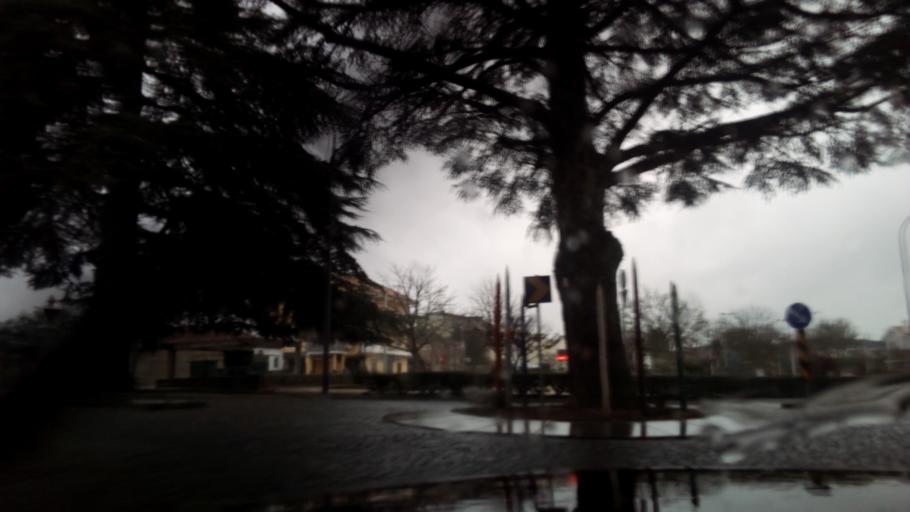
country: PT
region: Guarda
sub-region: Celorico da Beira
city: Celorico da Beira
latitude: 40.6337
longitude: -7.3937
